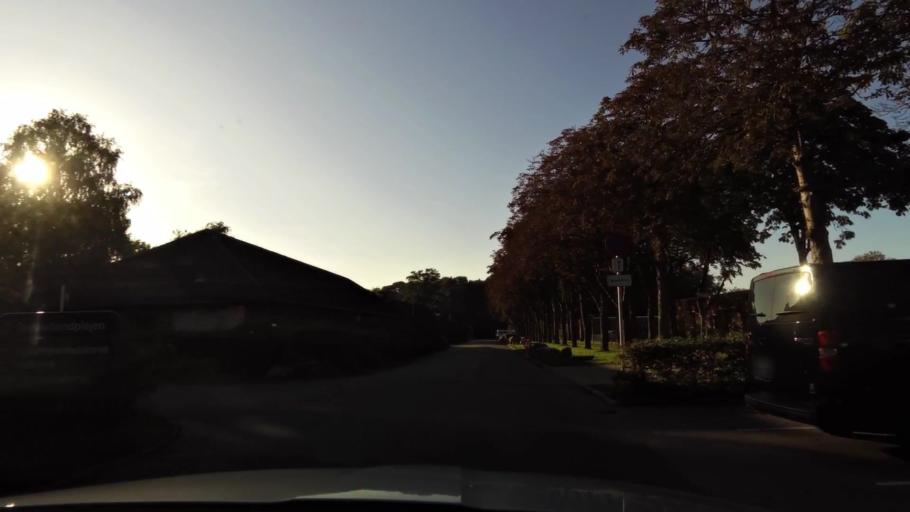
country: DK
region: Capital Region
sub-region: Lyngby-Tarbaek Kommune
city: Kongens Lyngby
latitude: 55.7519
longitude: 12.5099
